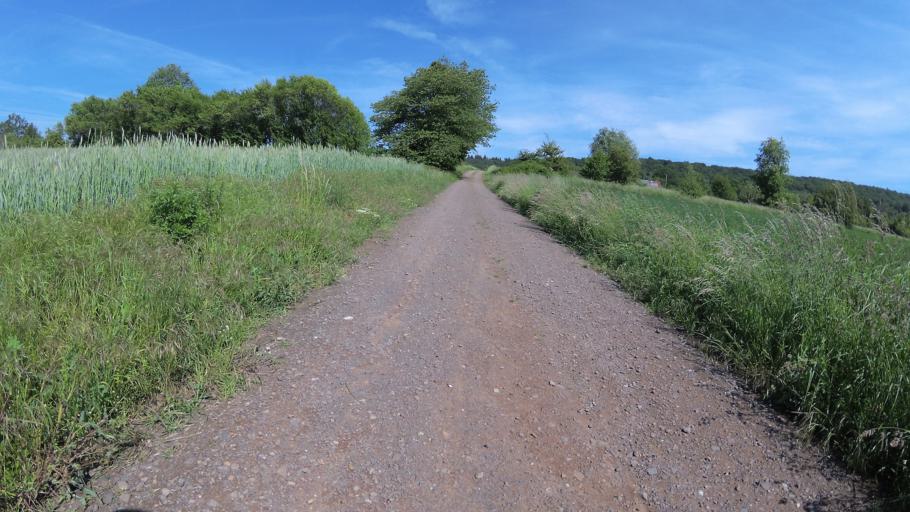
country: DE
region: Saarland
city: Ottweiler
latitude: 49.4331
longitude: 7.1712
